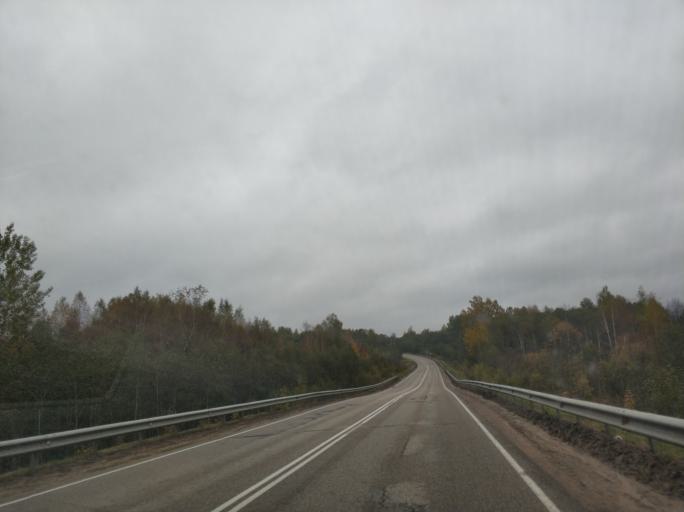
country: BY
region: Vitebsk
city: Rasony
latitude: 56.0582
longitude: 28.7141
